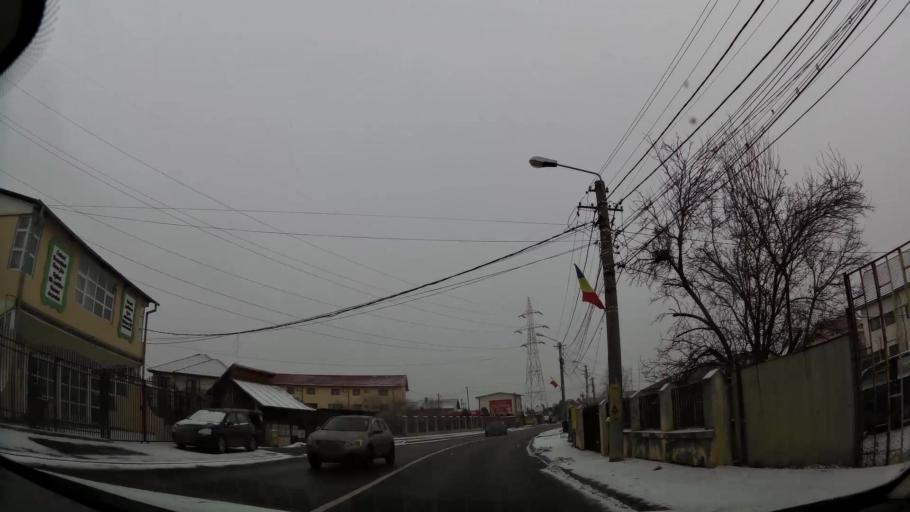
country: RO
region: Dambovita
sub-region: Municipiul Targoviste
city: Targoviste
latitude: 44.9305
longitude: 25.4714
